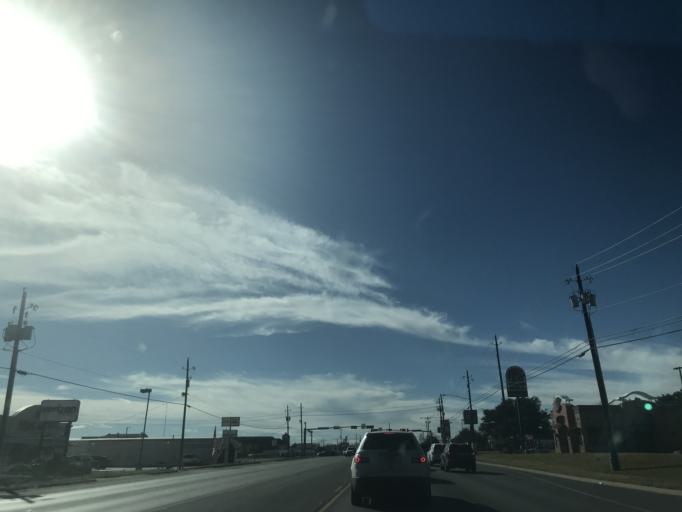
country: US
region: Texas
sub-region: Erath County
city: Stephenville
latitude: 32.2046
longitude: -98.2371
